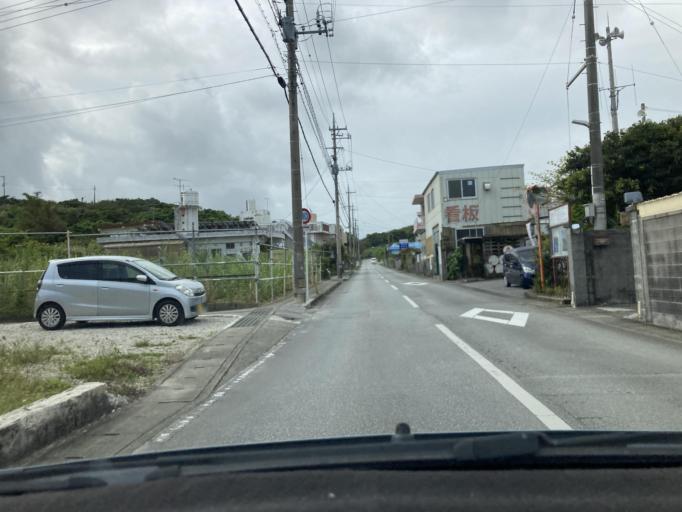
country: JP
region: Okinawa
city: Ginowan
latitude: 26.2323
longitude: 127.7438
